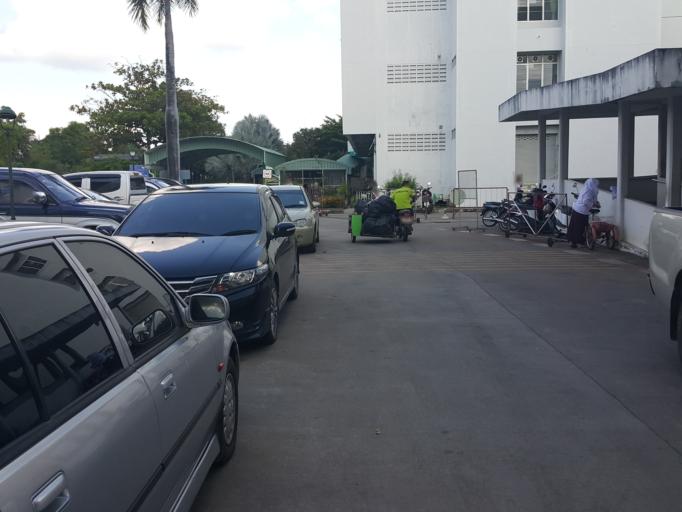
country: TH
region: Lampang
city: Lampang
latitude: 18.2881
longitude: 99.5058
